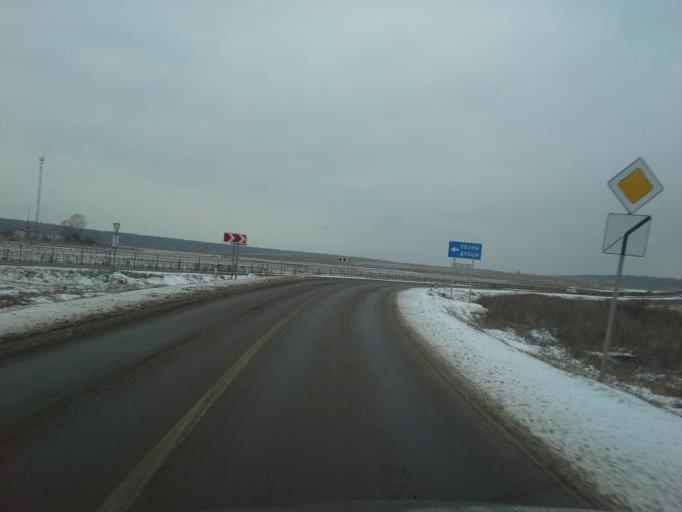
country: RU
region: Moskovskaya
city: Gorki Vtoryye
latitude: 55.7338
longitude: 37.1041
